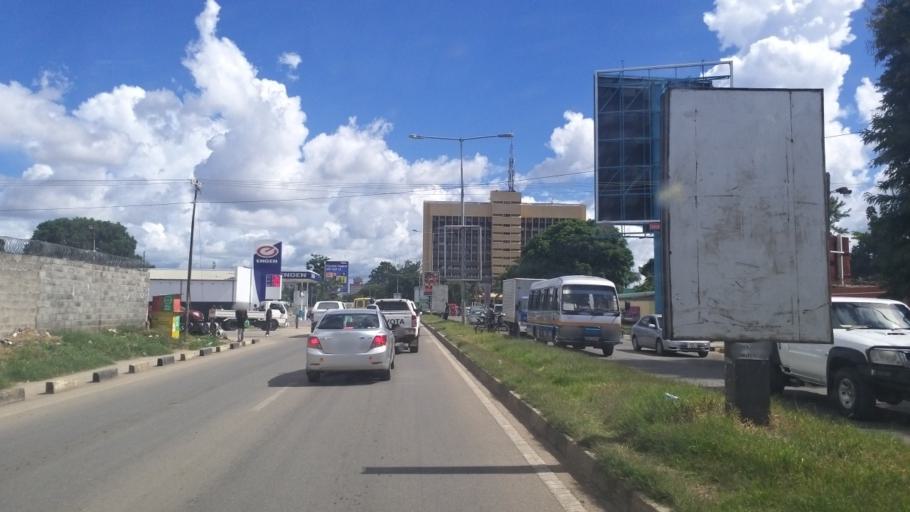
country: ZM
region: Lusaka
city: Lusaka
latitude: -15.4058
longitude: 28.2795
